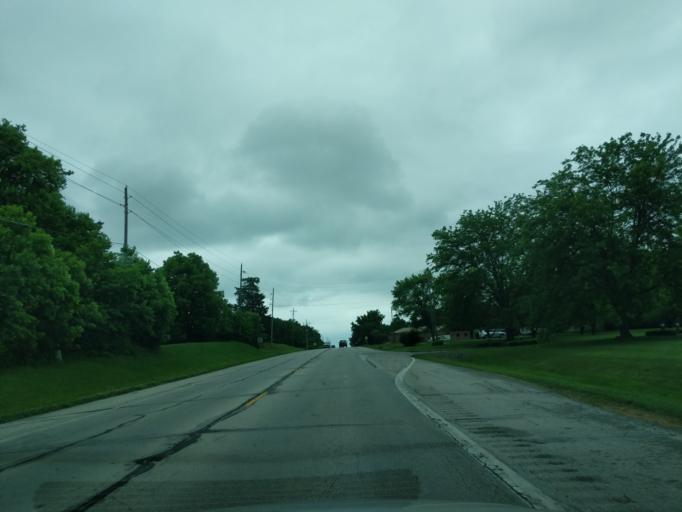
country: US
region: Indiana
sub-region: Hamilton County
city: Cicero
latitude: 40.1451
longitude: -86.0133
